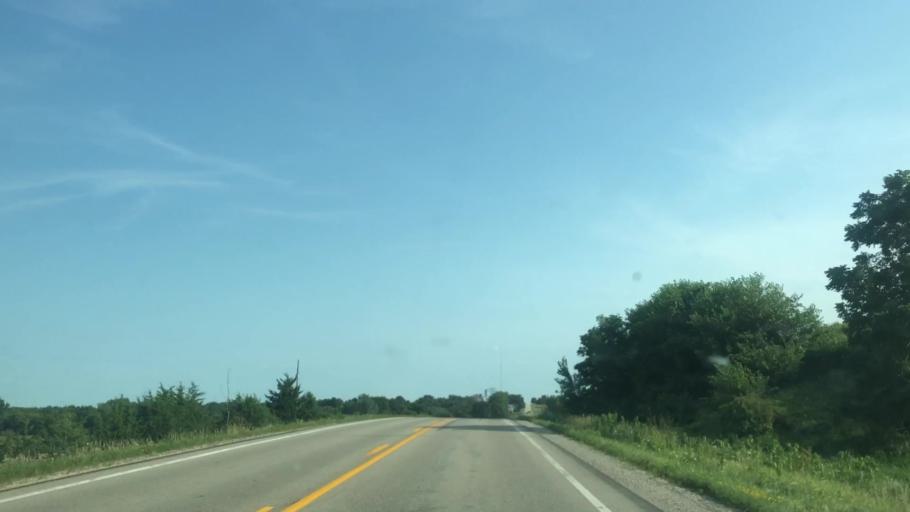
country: US
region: Iowa
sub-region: Marshall County
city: Marshalltown
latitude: 42.0352
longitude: -93.0000
